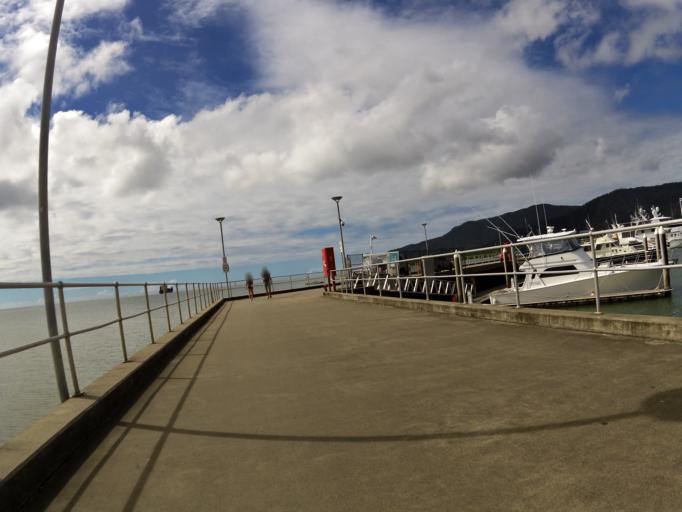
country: AU
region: Queensland
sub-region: Cairns
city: Cairns
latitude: -16.9173
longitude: 145.7810
